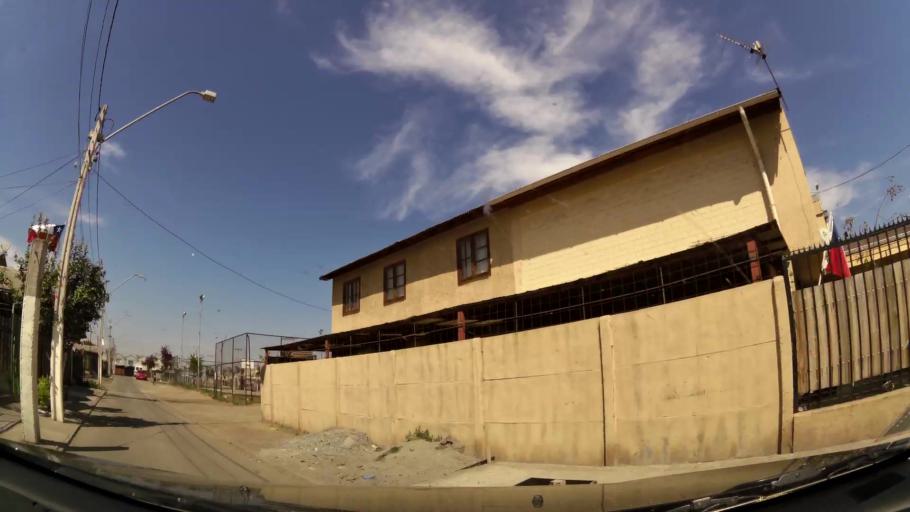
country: CL
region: Santiago Metropolitan
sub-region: Provincia de Santiago
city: Lo Prado
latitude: -33.4026
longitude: -70.7221
